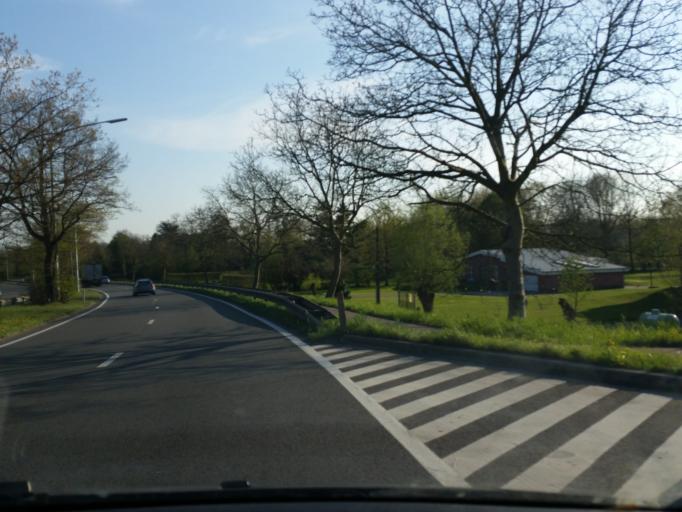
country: BE
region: Flanders
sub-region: Provincie Oost-Vlaanderen
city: Temse
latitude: 51.1173
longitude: 4.2176
